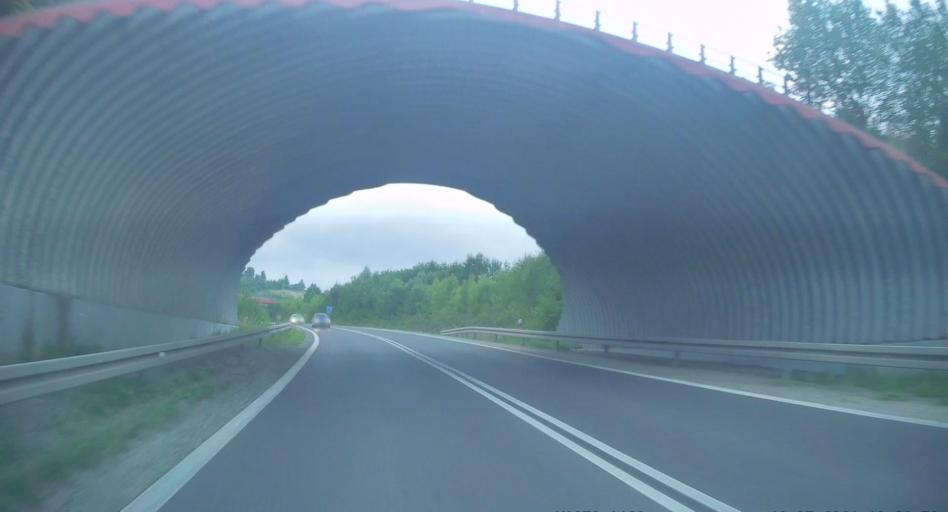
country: PL
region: Lower Silesian Voivodeship
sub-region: Powiat klodzki
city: Nowa Ruda
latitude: 50.5938
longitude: 16.5207
